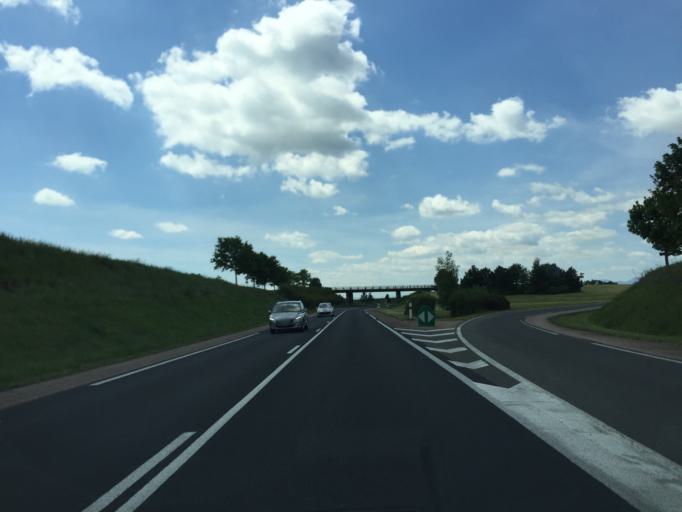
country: FR
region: Auvergne
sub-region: Departement du Puy-de-Dome
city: Aigueperse
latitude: 46.0166
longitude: 3.2131
